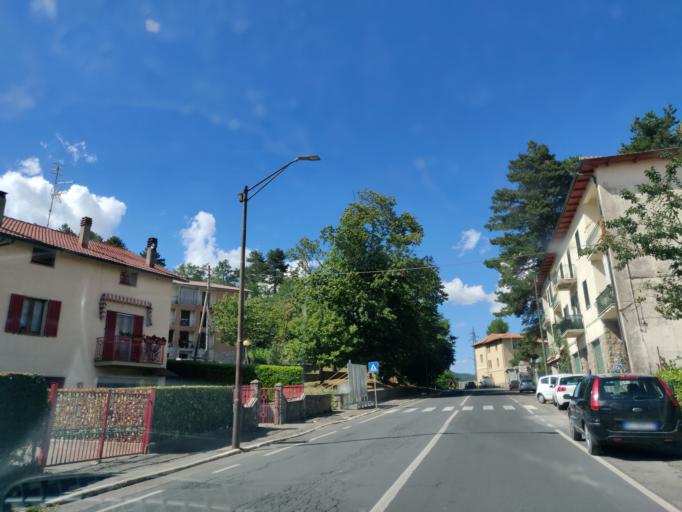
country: IT
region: Tuscany
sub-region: Provincia di Siena
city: Abbadia San Salvatore
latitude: 42.8847
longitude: 11.6701
